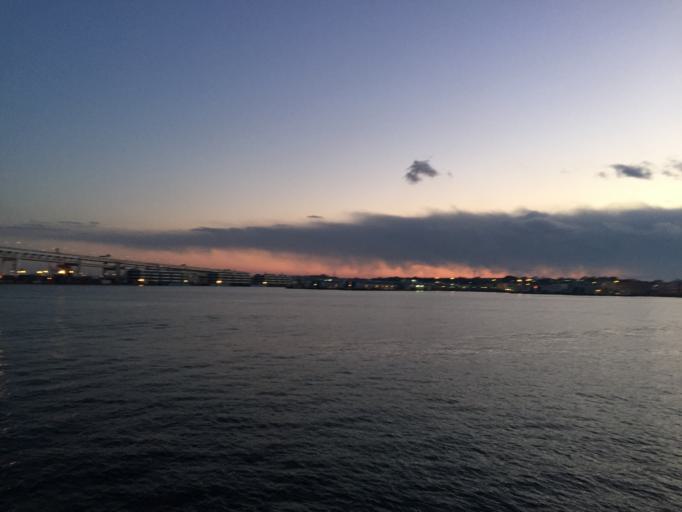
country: JP
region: Kanagawa
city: Yokohama
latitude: 35.4581
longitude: 139.6659
